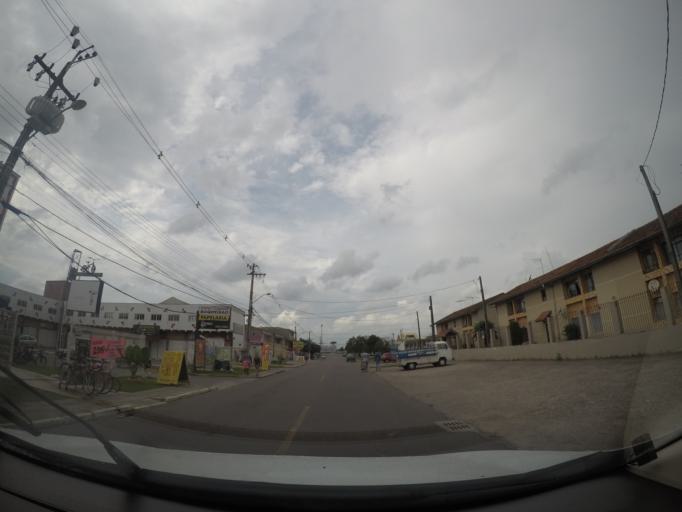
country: BR
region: Parana
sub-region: Sao Jose Dos Pinhais
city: Sao Jose dos Pinhais
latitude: -25.5051
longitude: -49.2199
